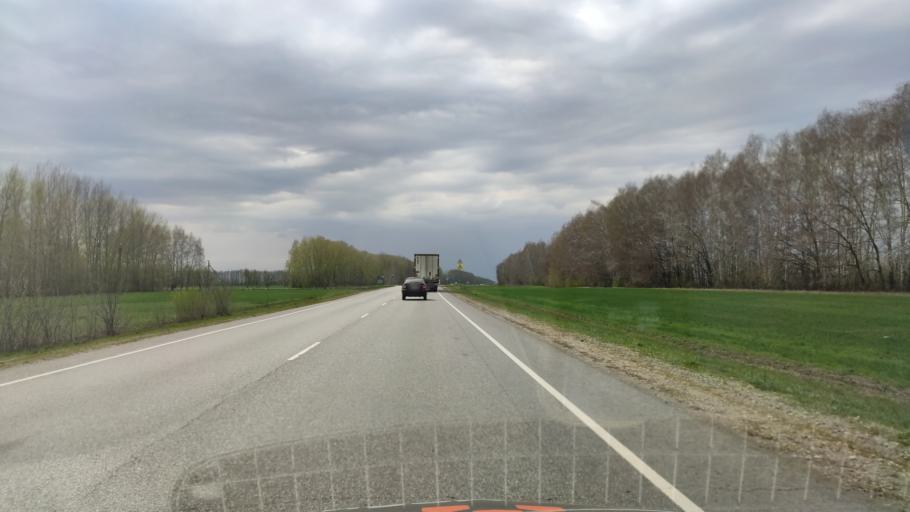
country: RU
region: Kursk
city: Olym
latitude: 51.5510
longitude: 38.2078
